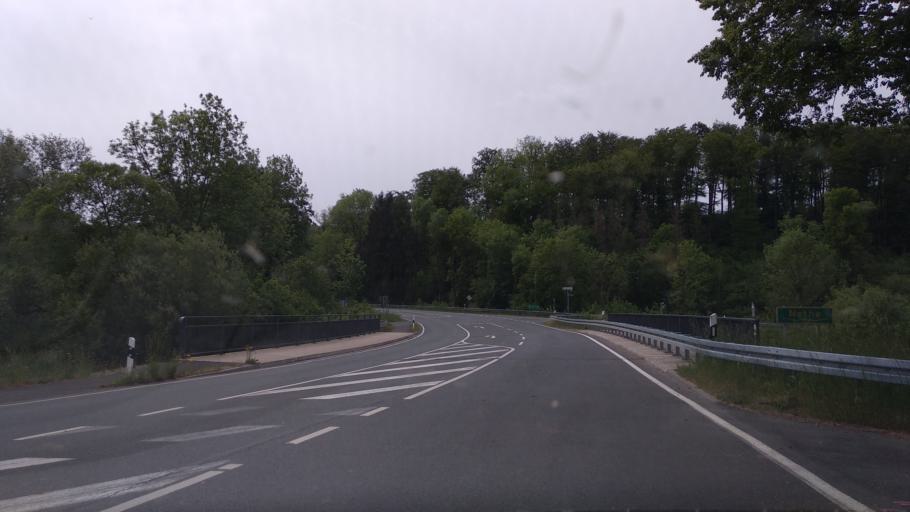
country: DE
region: North Rhine-Westphalia
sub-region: Regierungsbezirk Detmold
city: Willebadessen
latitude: 51.6243
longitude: 9.0991
